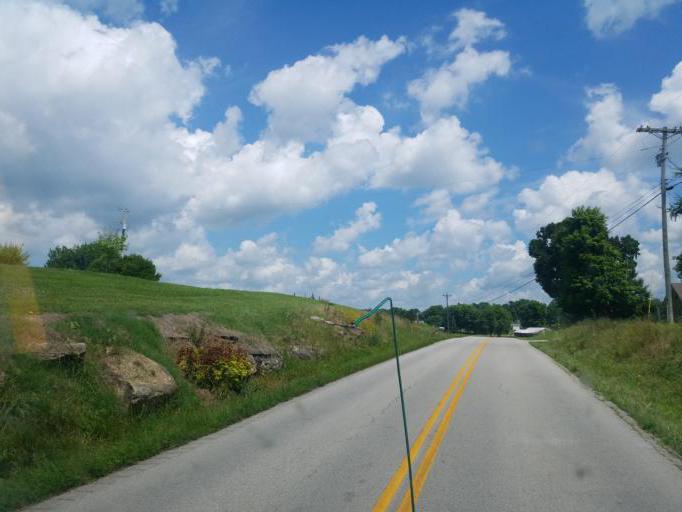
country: US
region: Kentucky
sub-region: Grayson County
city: Leitchfield
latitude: 37.5133
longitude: -86.3273
